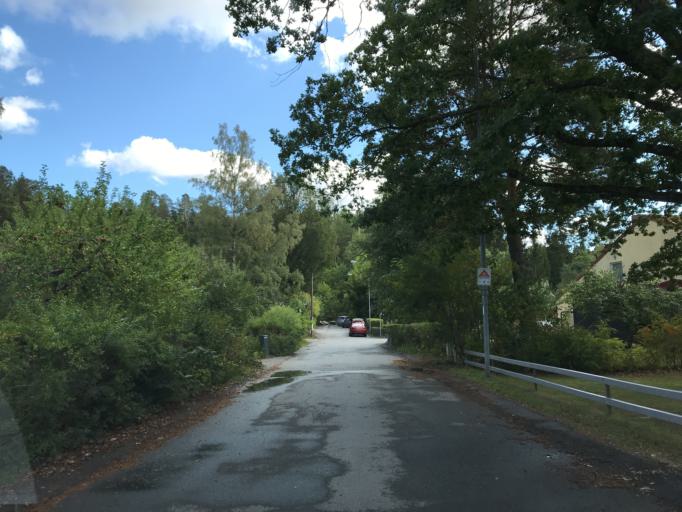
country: SE
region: Stockholm
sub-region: Sollentuna Kommun
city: Sollentuna
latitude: 59.4525
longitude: 17.9612
